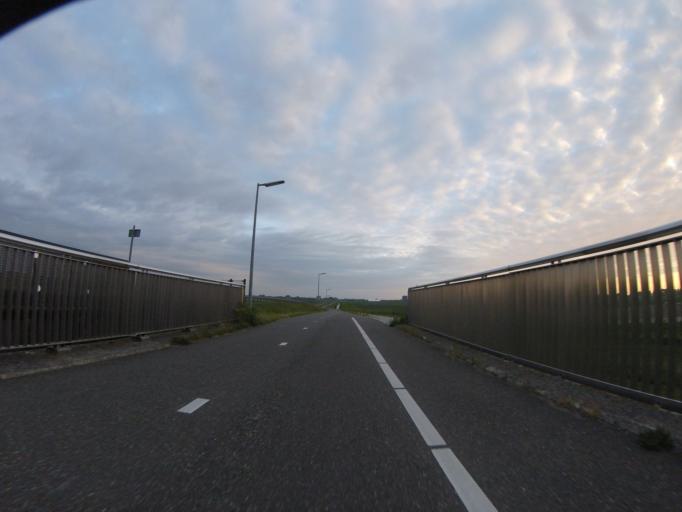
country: NL
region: North Holland
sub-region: Gemeente Haarlemmermeer
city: Hoofddorp
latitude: 52.2900
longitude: 4.6491
